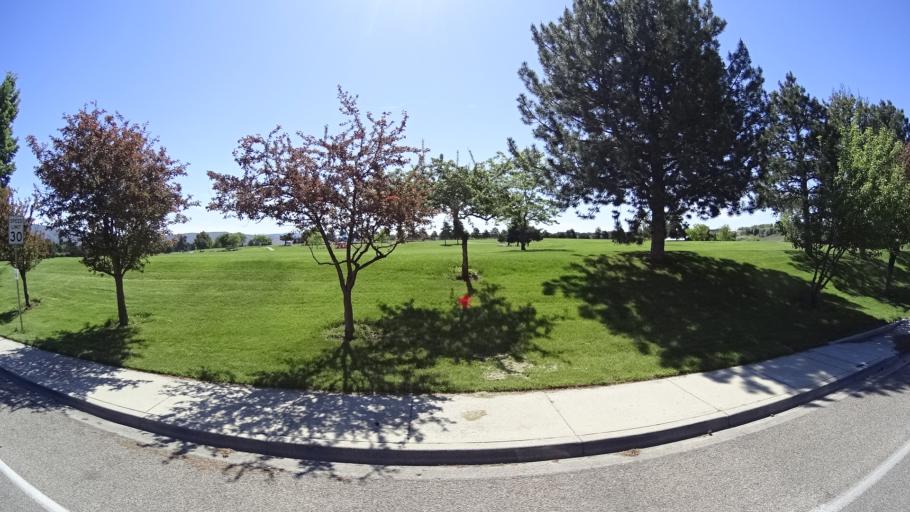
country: US
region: Idaho
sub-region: Ada County
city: Boise
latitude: 43.5493
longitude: -116.1532
